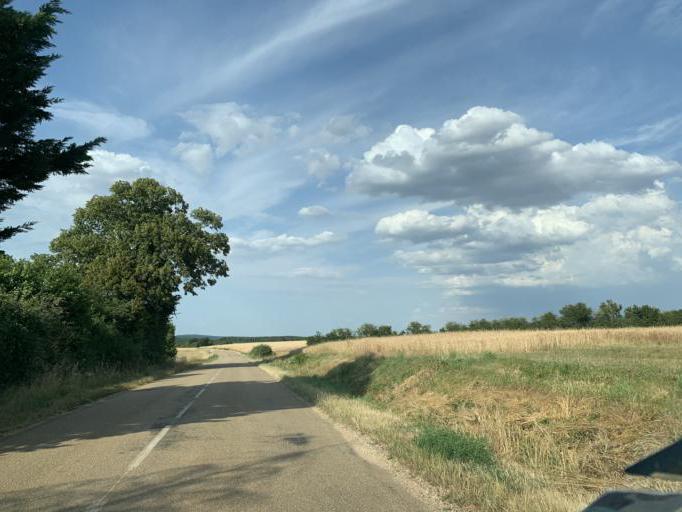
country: FR
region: Bourgogne
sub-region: Departement de l'Yonne
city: Fontenailles
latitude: 47.5249
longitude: 3.3839
